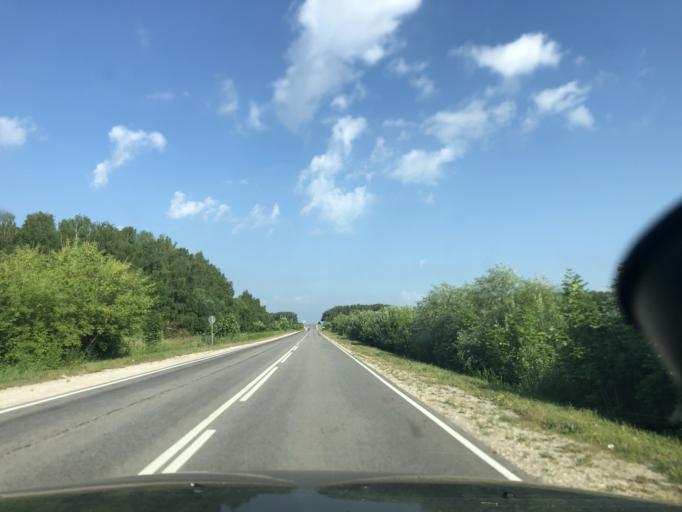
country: RU
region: Tula
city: Dubna
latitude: 54.1355
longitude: 37.0224
